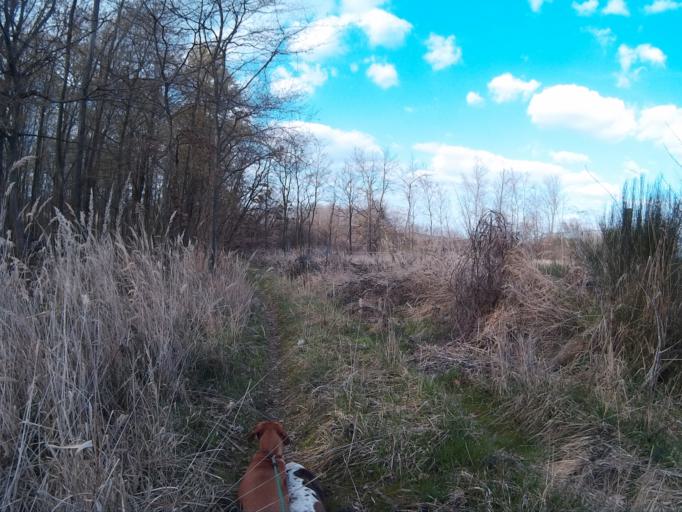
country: HU
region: Vas
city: Sarvar
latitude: 47.2036
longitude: 16.9896
